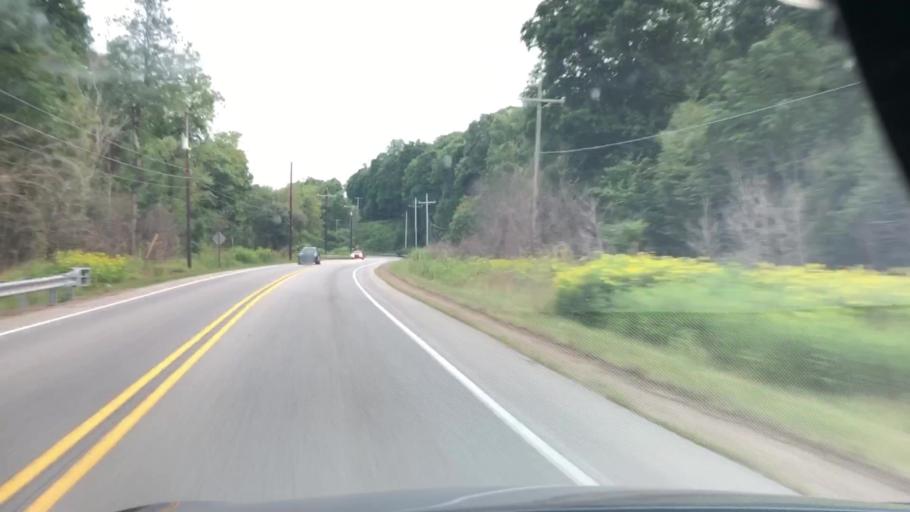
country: US
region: Pennsylvania
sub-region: Venango County
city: Hasson Heights
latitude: 41.4916
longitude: -79.7002
